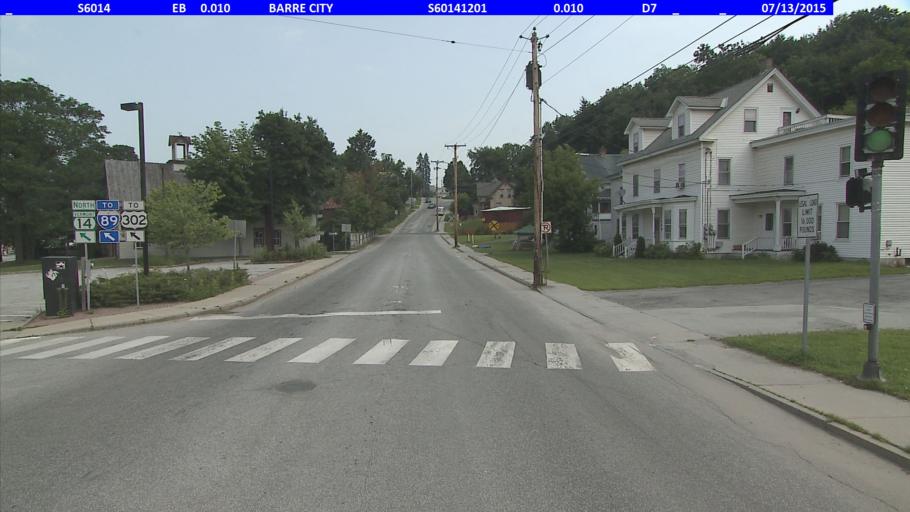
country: US
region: Vermont
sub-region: Washington County
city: Barre
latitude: 44.1909
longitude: -72.4987
